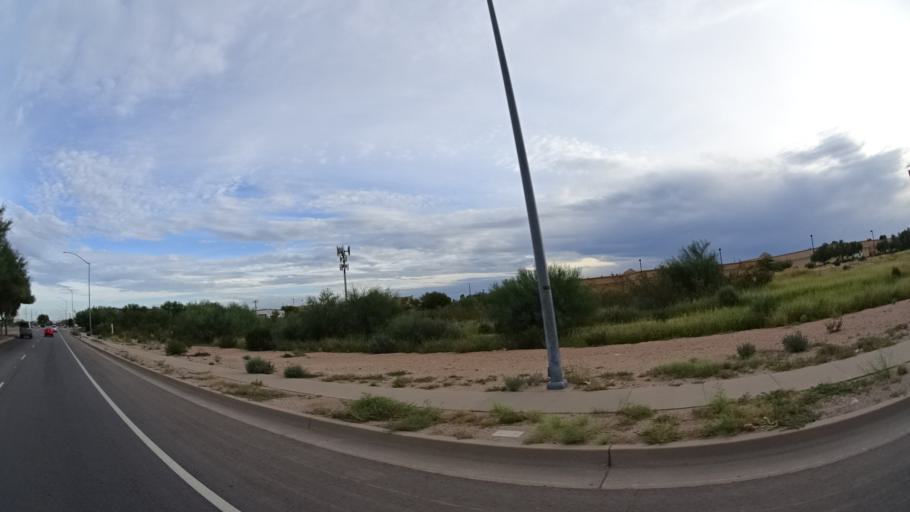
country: US
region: Arizona
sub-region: Pima County
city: South Tucson
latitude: 32.1660
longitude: -110.9400
